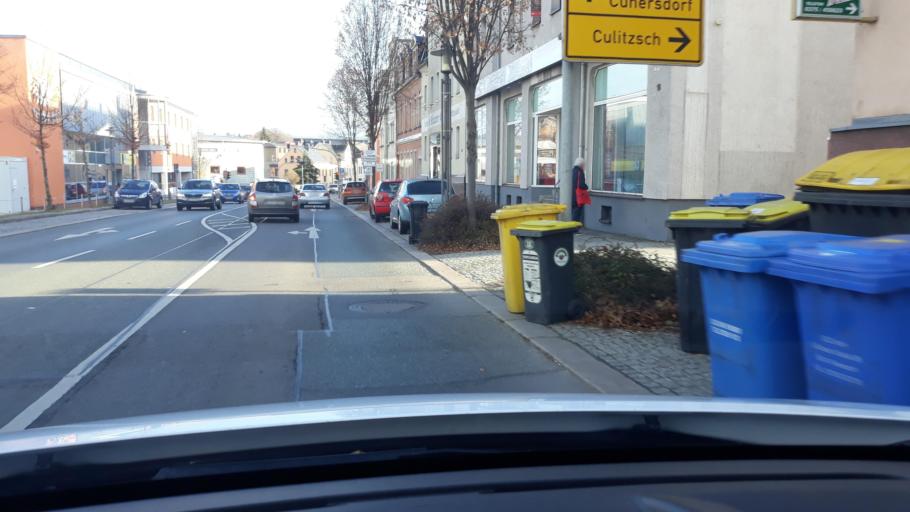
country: DE
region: Saxony
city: Wilkau-Hasslau
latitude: 50.6745
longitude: 12.5137
